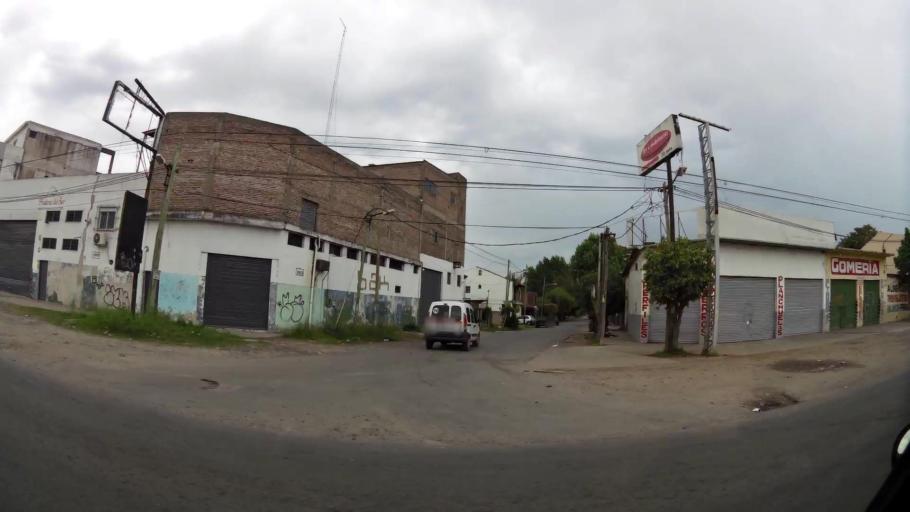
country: AR
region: Buenos Aires
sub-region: Partido de Quilmes
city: Quilmes
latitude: -34.7860
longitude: -58.2527
